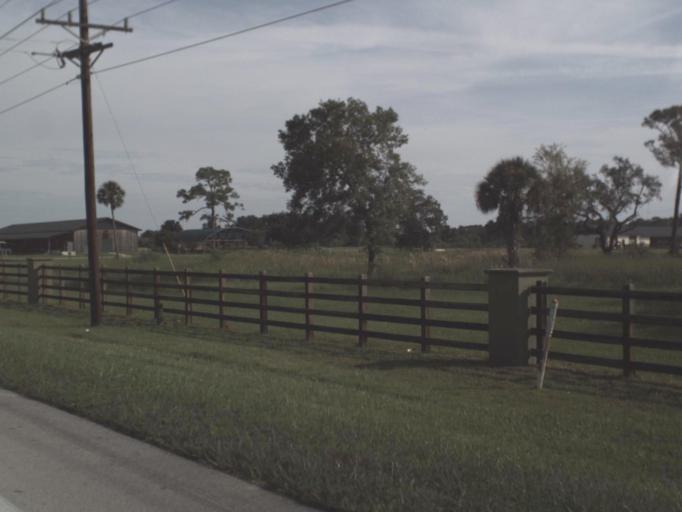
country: US
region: Florida
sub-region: Lee County
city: Fort Myers Shores
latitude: 26.7339
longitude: -81.7610
